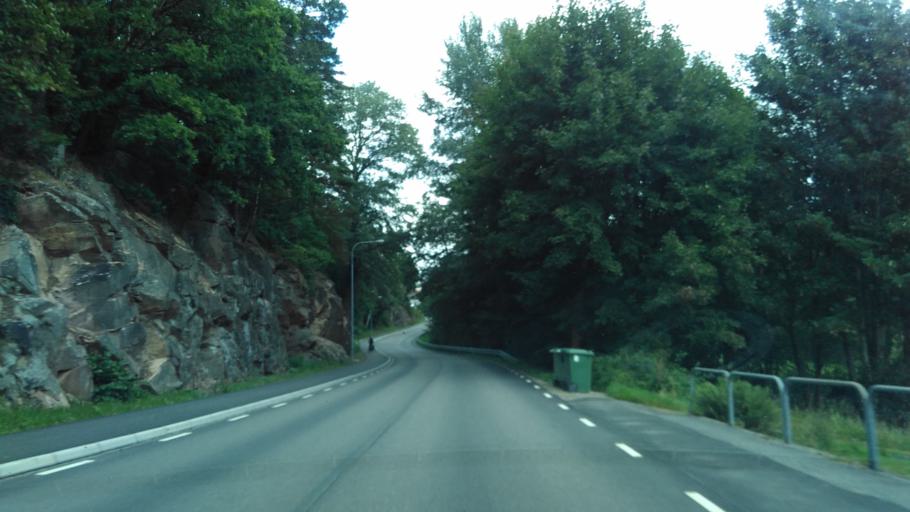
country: SE
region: Vaestra Goetaland
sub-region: Marks Kommun
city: Fritsla
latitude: 57.5608
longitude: 12.7849
